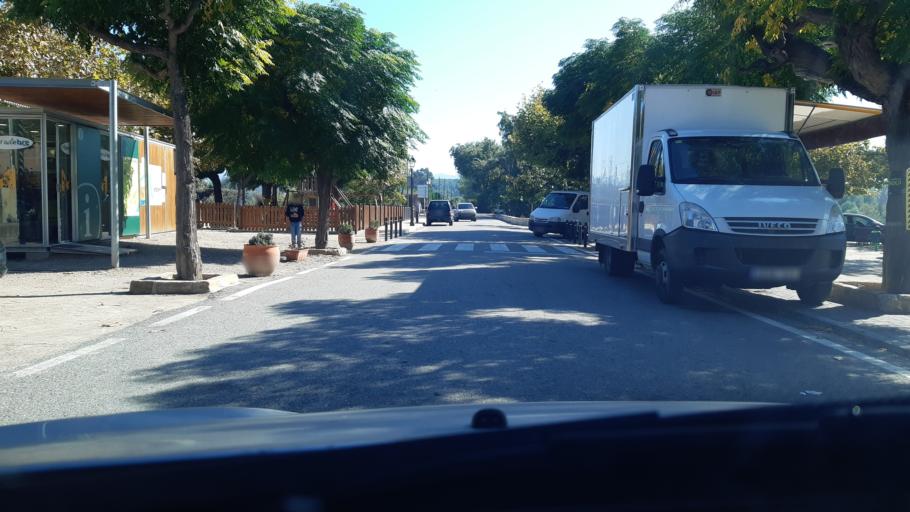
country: ES
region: Catalonia
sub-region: Provincia de Tarragona
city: Miravet
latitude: 41.0376
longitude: 0.5983
